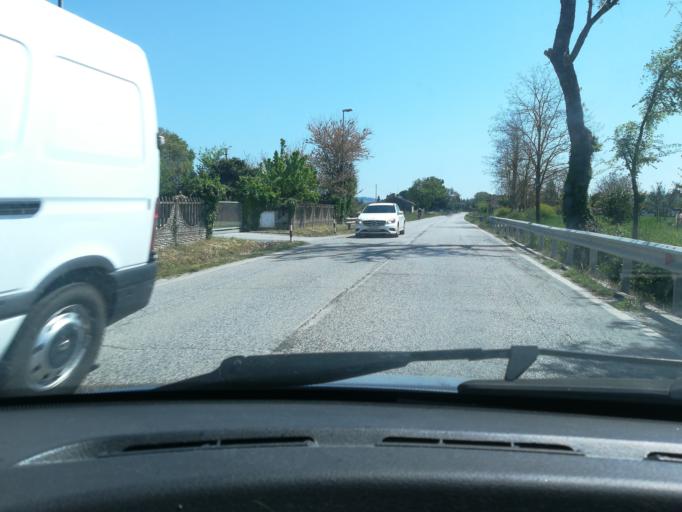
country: IT
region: The Marches
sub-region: Provincia di Ancona
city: Castelfidardo
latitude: 43.4537
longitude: 13.5261
